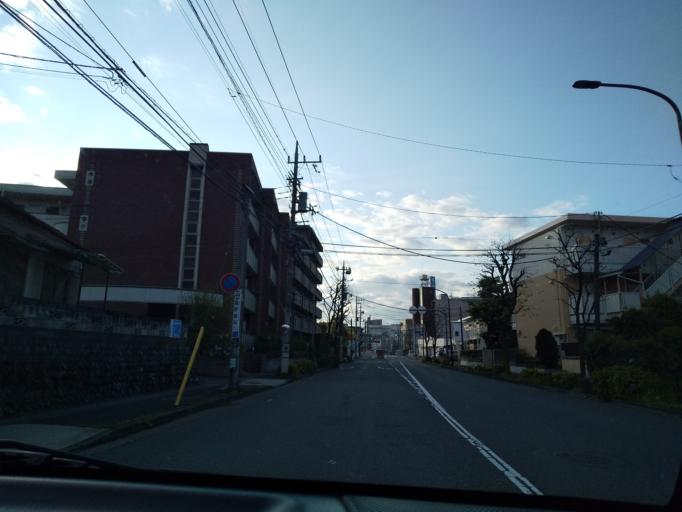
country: JP
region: Tokyo
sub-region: Machida-shi
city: Machida
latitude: 35.5490
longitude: 139.4359
